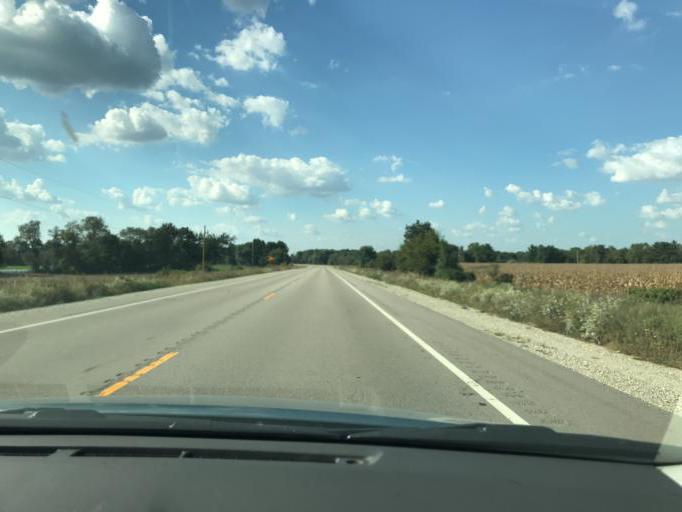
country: US
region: Wisconsin
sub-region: Green County
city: Brodhead
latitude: 42.5810
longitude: -89.3794
